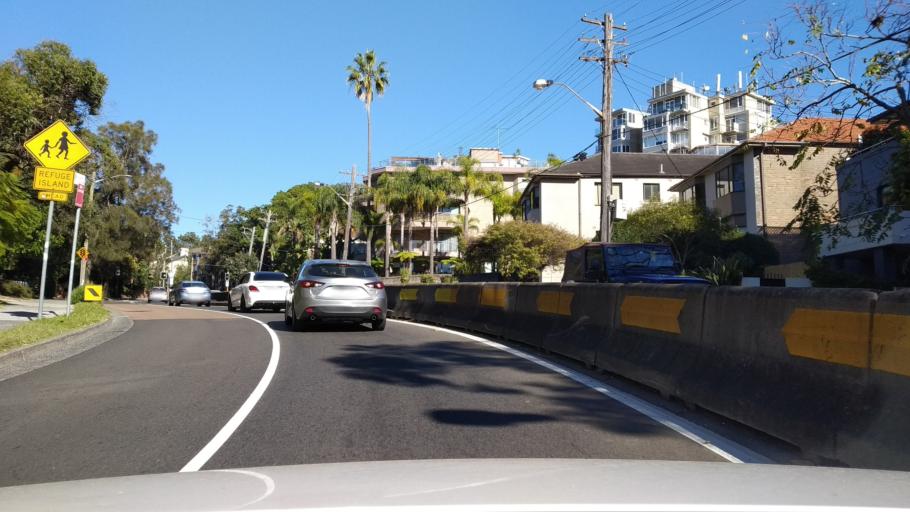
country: AU
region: New South Wales
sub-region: Waverley
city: Bondi
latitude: -33.8885
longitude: 151.2603
